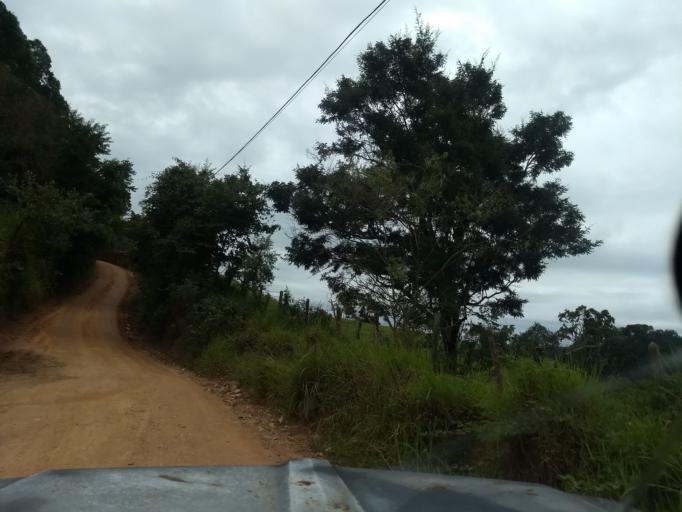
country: BR
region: Sao Paulo
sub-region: Cabreuva
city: Cabreuva
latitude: -23.4003
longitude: -47.1941
